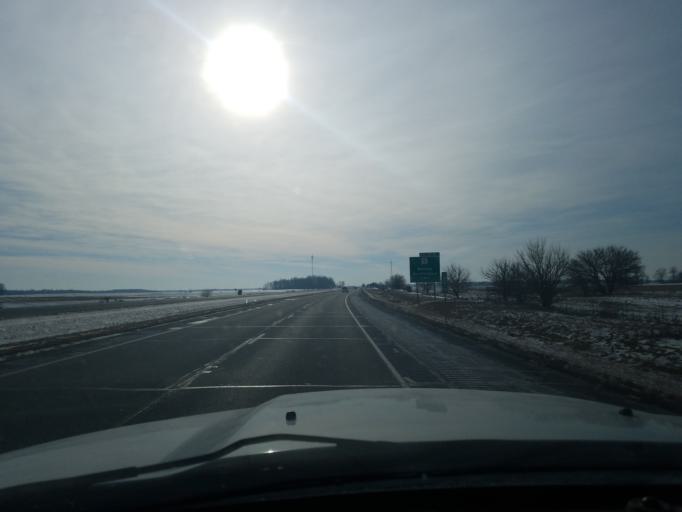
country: US
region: Indiana
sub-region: Huntington County
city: Warren
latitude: 40.7355
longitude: -85.4174
